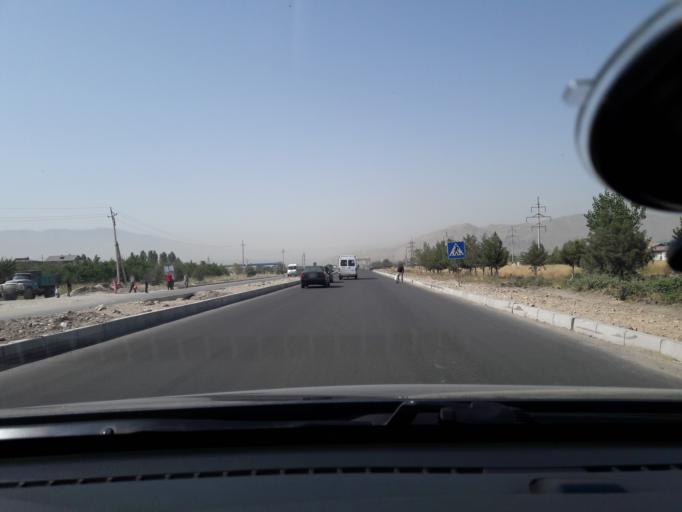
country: TJ
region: Dushanbe
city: Boshkengash
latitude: 38.4796
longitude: 68.7461
